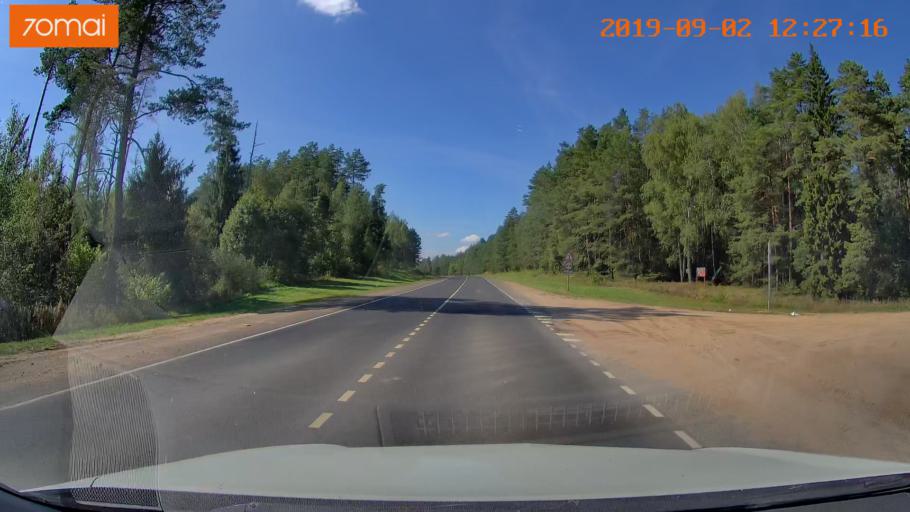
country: RU
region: Smolensk
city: Shumyachi
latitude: 53.8541
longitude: 32.5485
